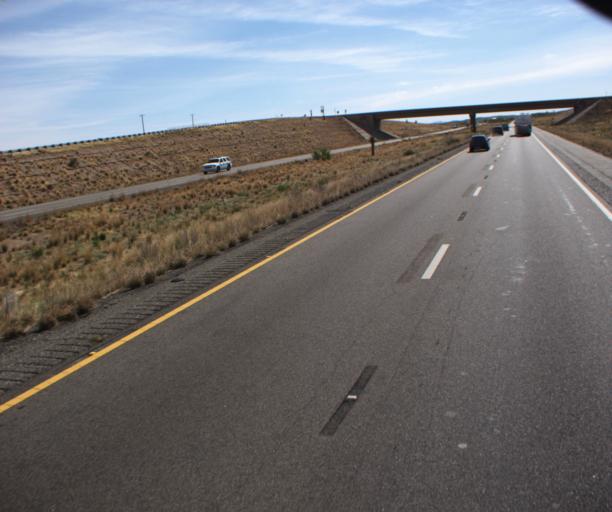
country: US
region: Arizona
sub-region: Cochise County
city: Mescal
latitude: 31.9820
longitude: -110.5389
